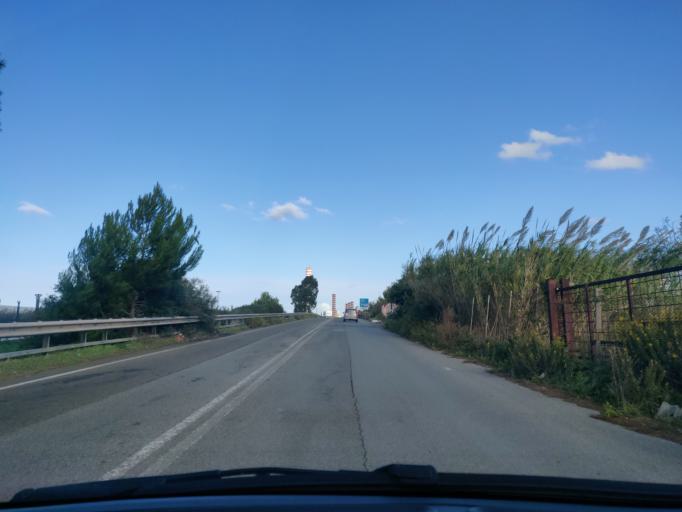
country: IT
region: Latium
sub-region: Citta metropolitana di Roma Capitale
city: Aurelia
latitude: 42.1135
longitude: 11.7746
